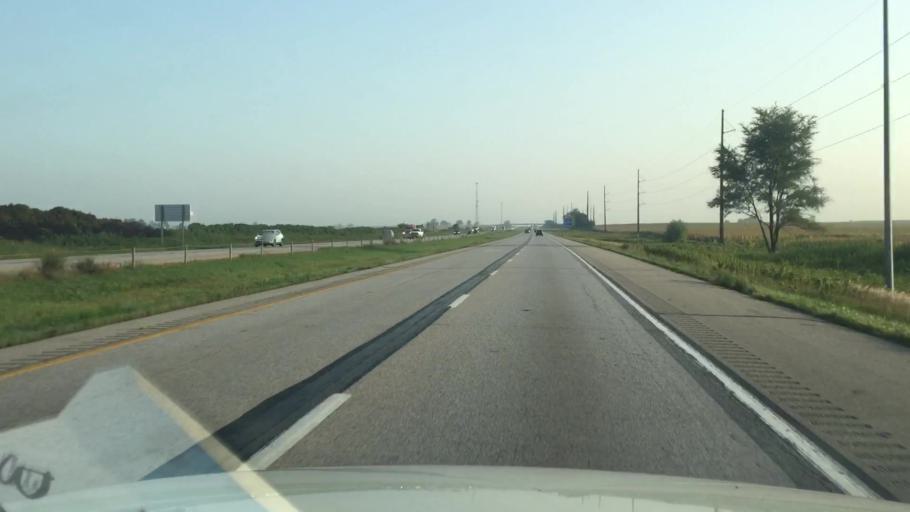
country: US
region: Iowa
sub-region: Polk County
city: Ankeny
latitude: 41.8058
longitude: -93.5702
